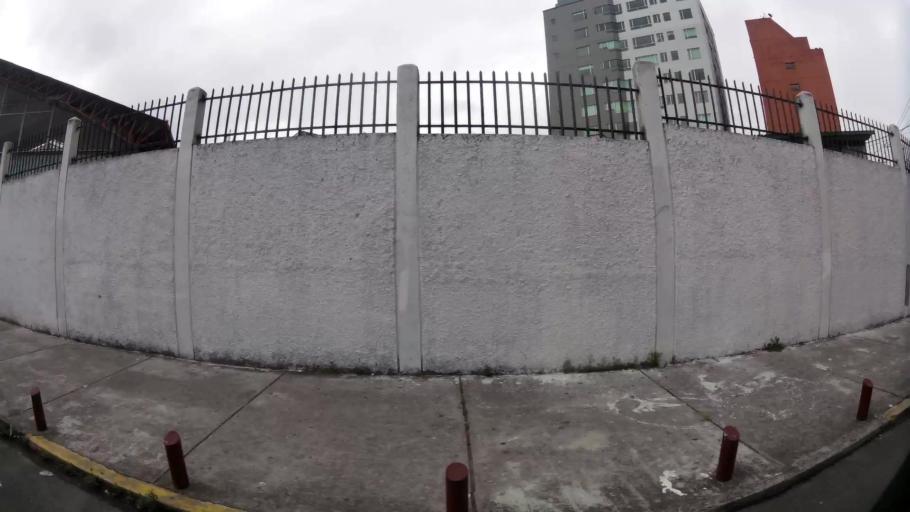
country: EC
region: Pichincha
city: Quito
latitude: -0.1956
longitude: -78.4925
